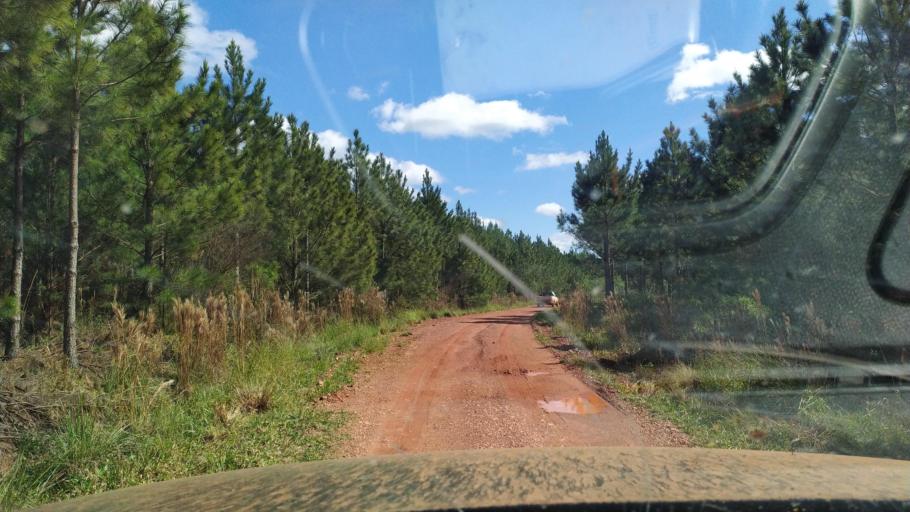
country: AR
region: Corrientes
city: Santo Tome
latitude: -28.4634
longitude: -55.9815
